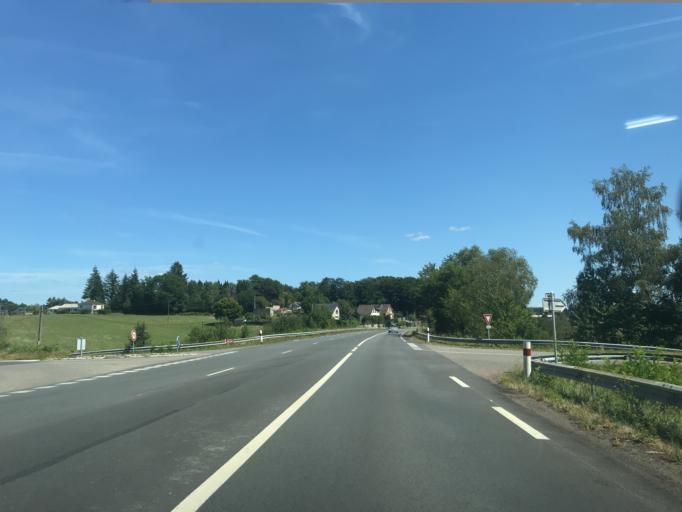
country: FR
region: Limousin
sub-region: Departement de la Correze
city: Correze
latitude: 45.3292
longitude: 1.8683
